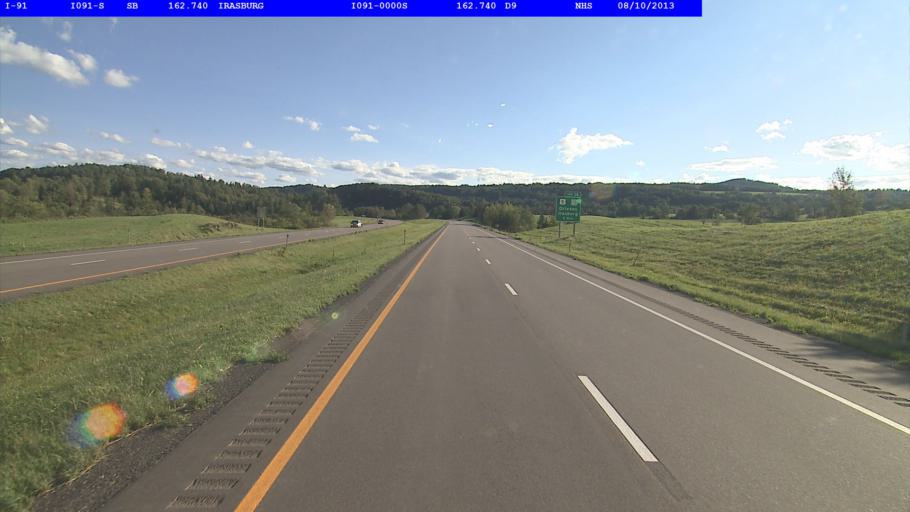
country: US
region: Vermont
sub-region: Orleans County
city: Newport
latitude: 44.8247
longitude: -72.2059
